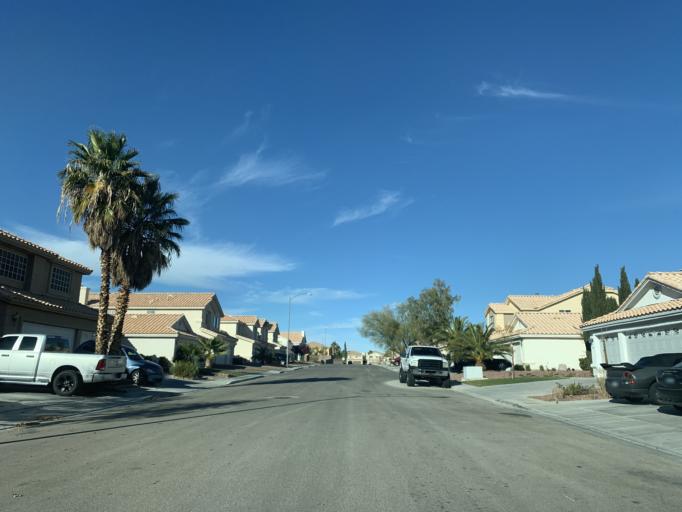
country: US
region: Nevada
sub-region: Clark County
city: Summerlin South
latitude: 36.1209
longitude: -115.3075
